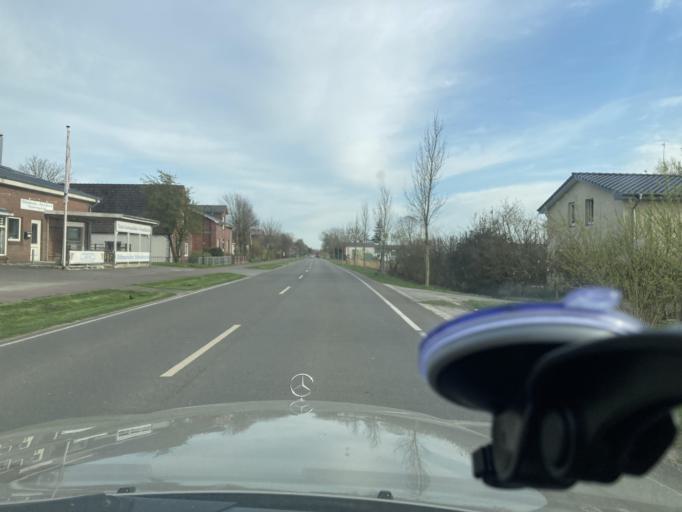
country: DE
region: Schleswig-Holstein
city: Krempel
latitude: 54.3188
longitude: 9.0282
